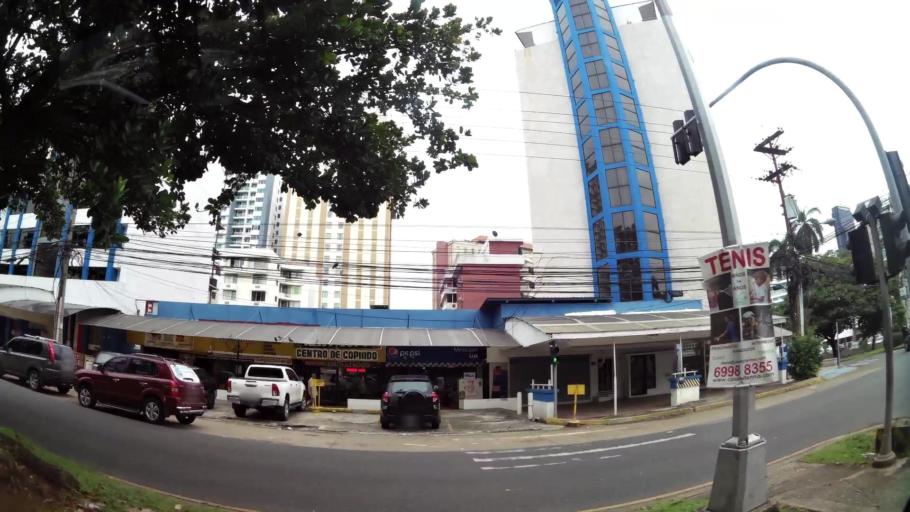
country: PA
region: Panama
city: Panama
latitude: 8.9837
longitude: -79.5301
